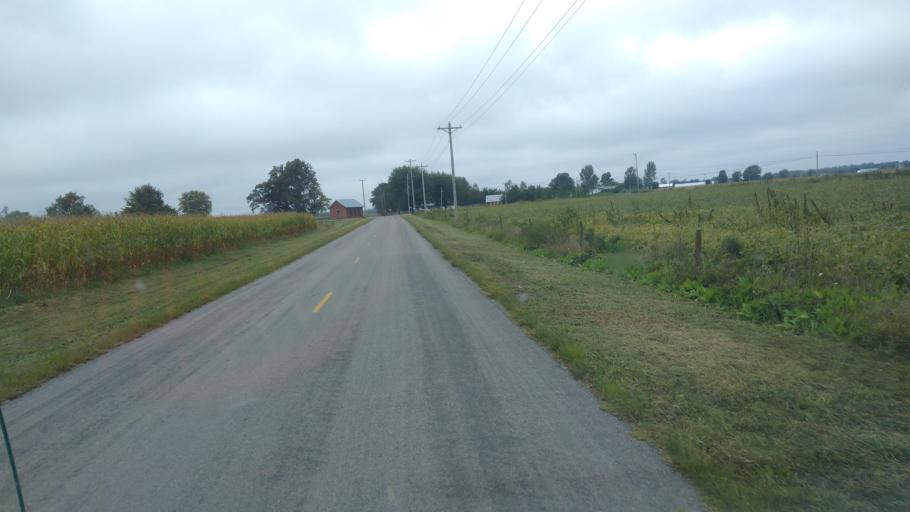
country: US
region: Ohio
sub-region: Hardin County
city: Kenton
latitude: 40.5725
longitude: -83.6505
